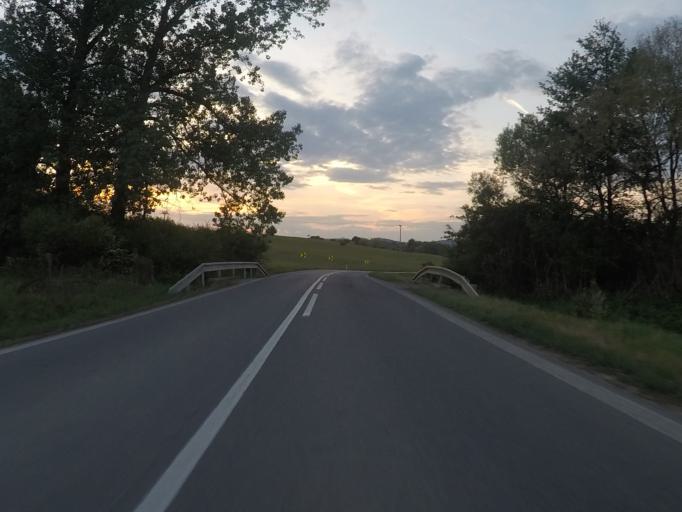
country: SK
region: Banskobystricky
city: Rimavska Sobota
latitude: 48.4542
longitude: 19.9551
